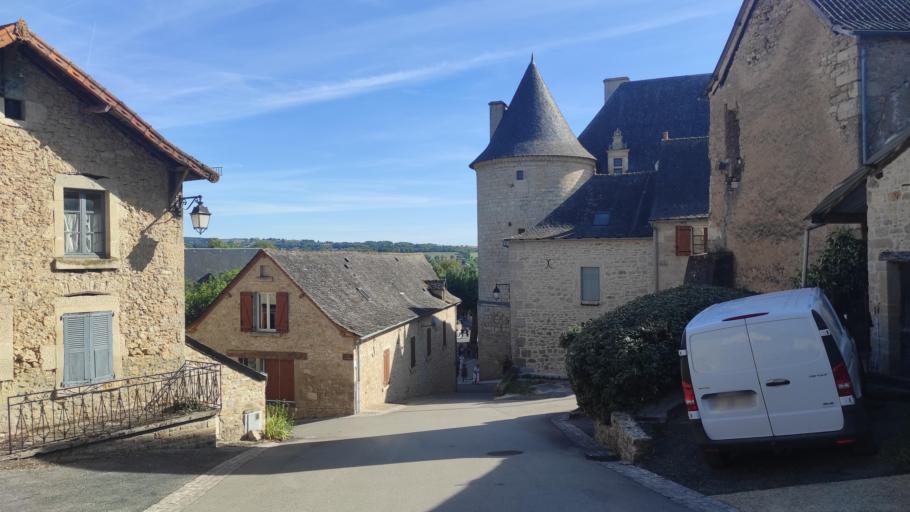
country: FR
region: Midi-Pyrenees
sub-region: Departement de l'Aveyron
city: Cransac
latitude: 44.4603
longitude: 2.2990
